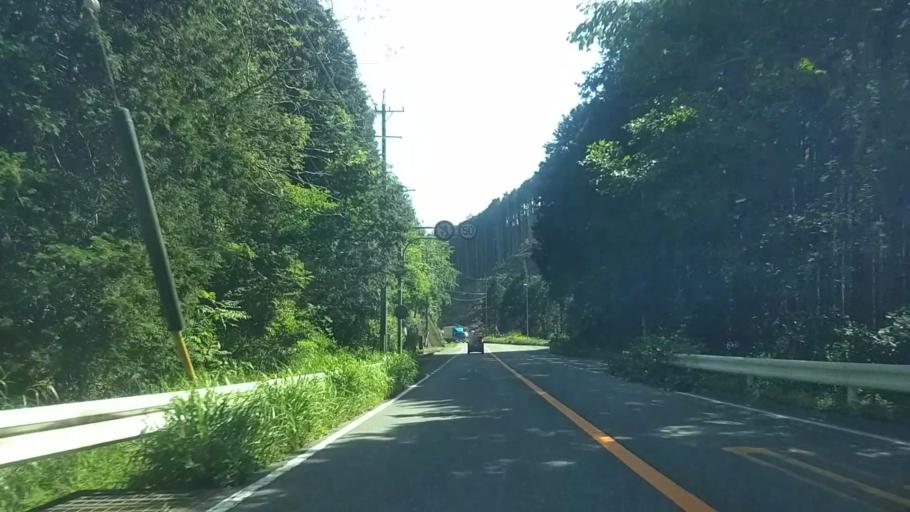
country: JP
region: Shizuoka
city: Fujinomiya
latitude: 35.1828
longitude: 138.5267
